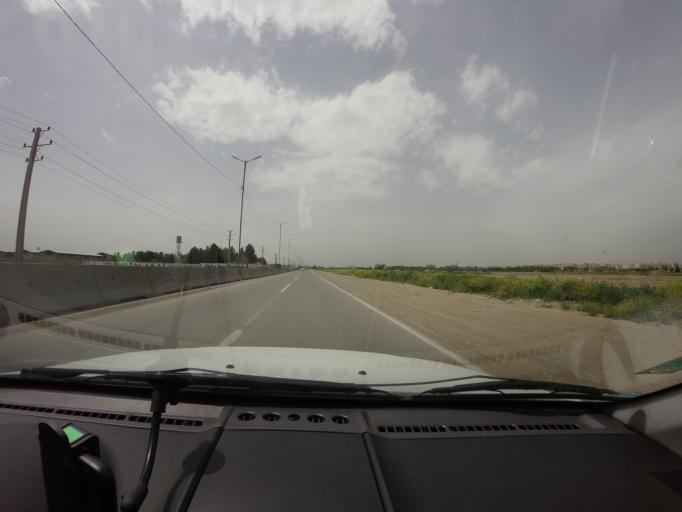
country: IR
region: Tehran
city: Eslamshahr
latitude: 35.5122
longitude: 51.2485
